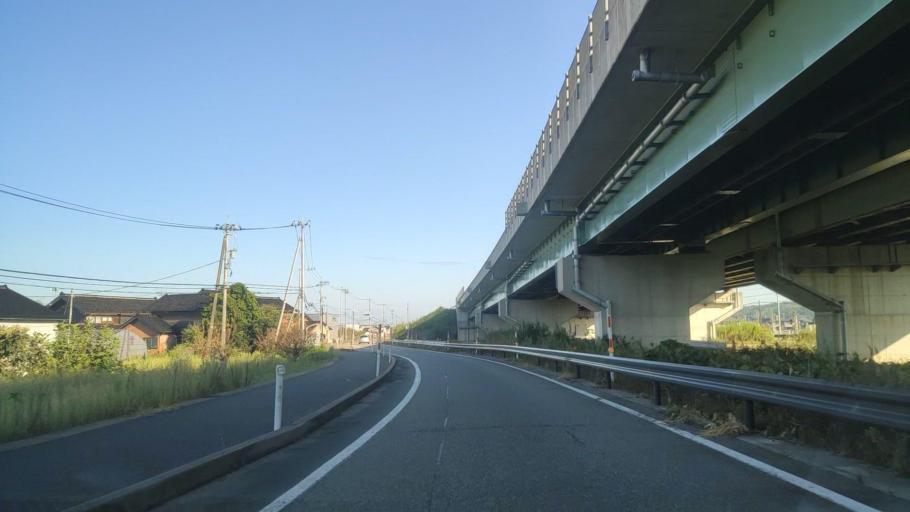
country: JP
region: Ishikawa
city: Tsubata
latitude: 36.6860
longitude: 136.7227
